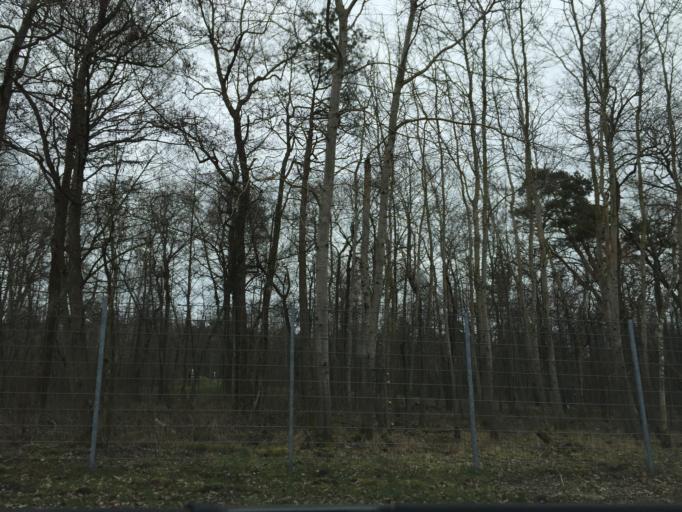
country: LT
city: Nida
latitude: 55.2815
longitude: 20.9660
